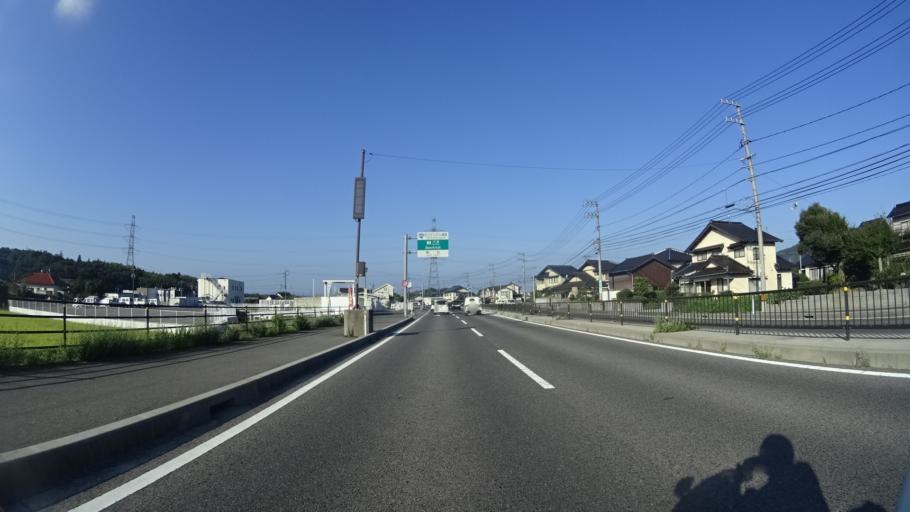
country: JP
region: Shimane
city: Matsue-shi
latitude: 35.5053
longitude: 133.0943
